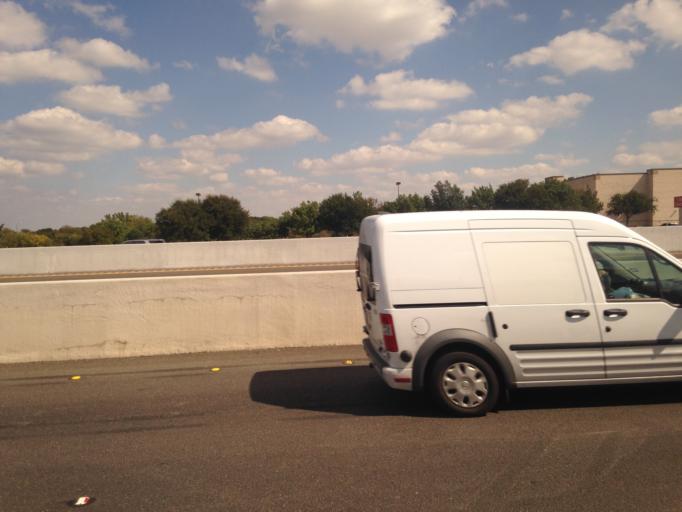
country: US
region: Texas
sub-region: Tarrant County
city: Blue Mound
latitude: 32.8553
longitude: -97.3136
